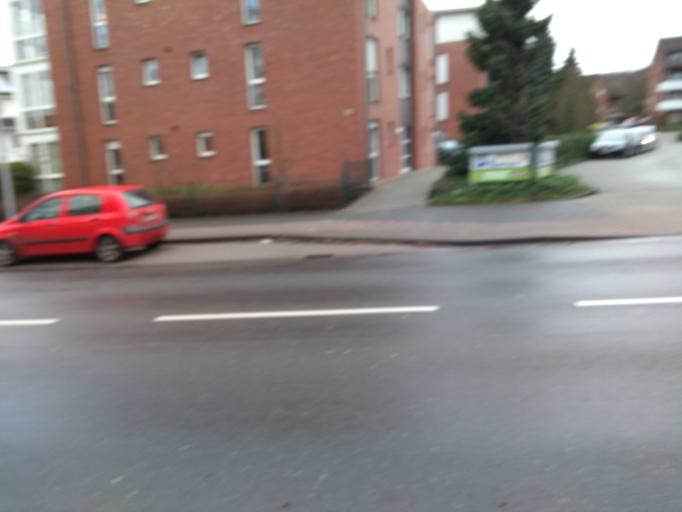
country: DE
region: North Rhine-Westphalia
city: Ibbenburen
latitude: 52.2794
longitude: 7.7112
